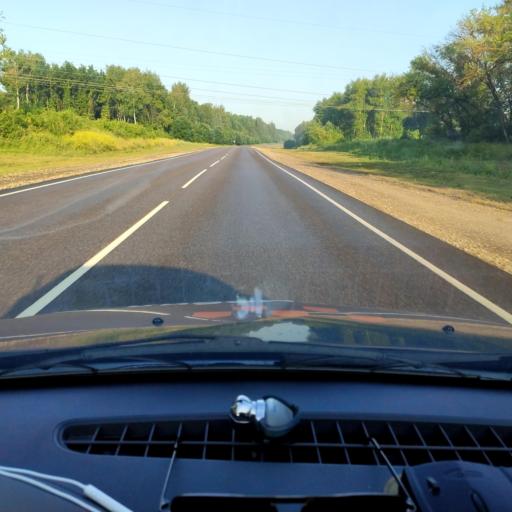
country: RU
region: Lipetsk
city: Kazaki
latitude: 52.6295
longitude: 38.3665
